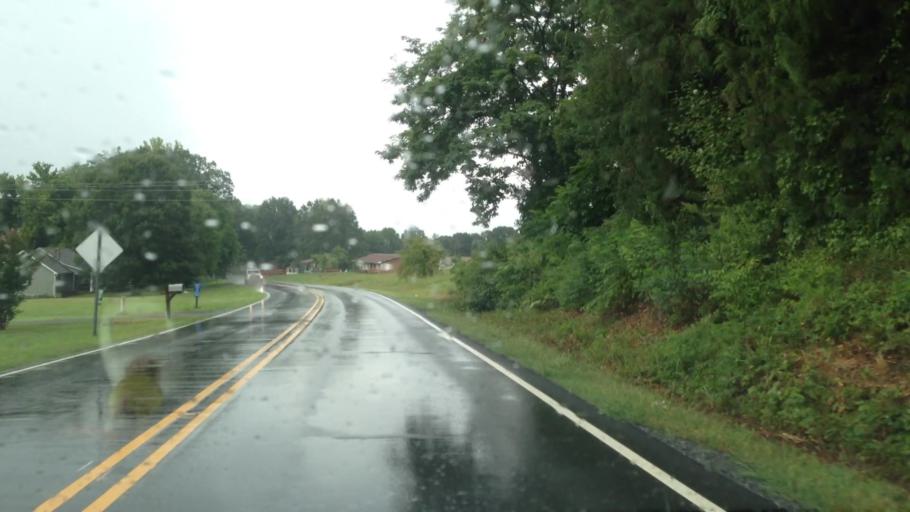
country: US
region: North Carolina
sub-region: Stokes County
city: Danbury
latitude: 36.4462
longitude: -80.1052
